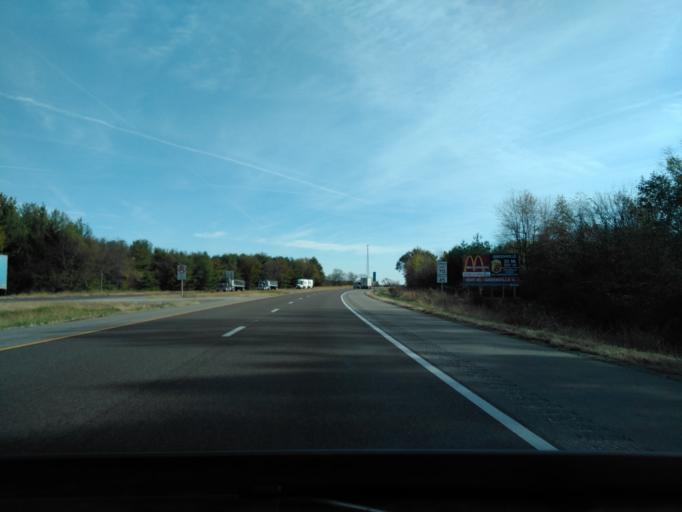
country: US
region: Illinois
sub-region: Madison County
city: Saint Jacob
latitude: 38.7829
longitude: -89.7349
